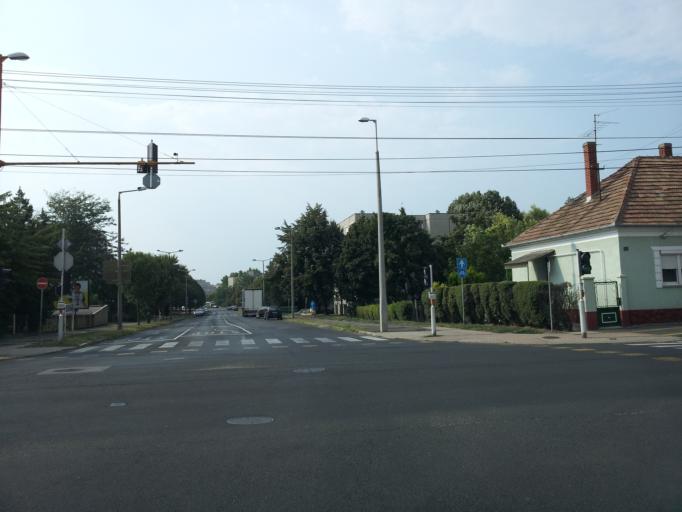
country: HU
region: Gyor-Moson-Sopron
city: Gyor
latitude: 47.6648
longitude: 17.6632
